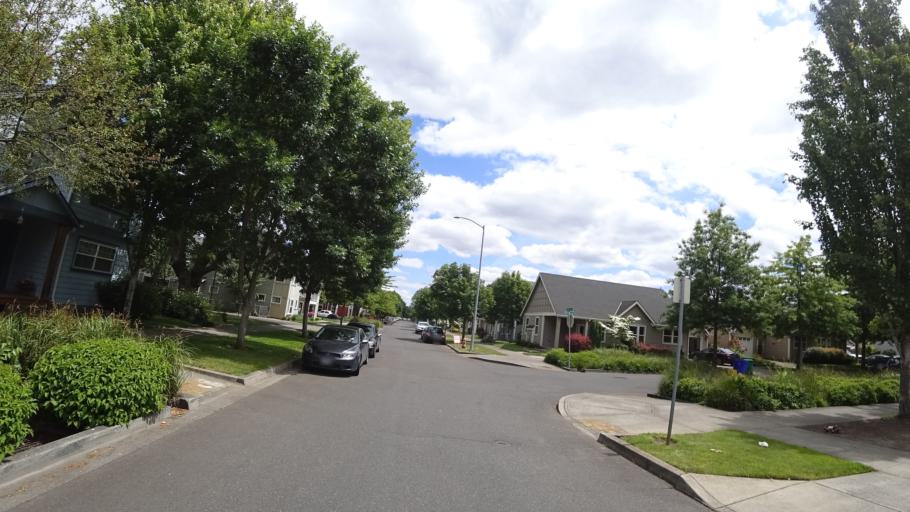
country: US
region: Oregon
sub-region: Multnomah County
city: Portland
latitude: 45.5872
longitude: -122.7165
